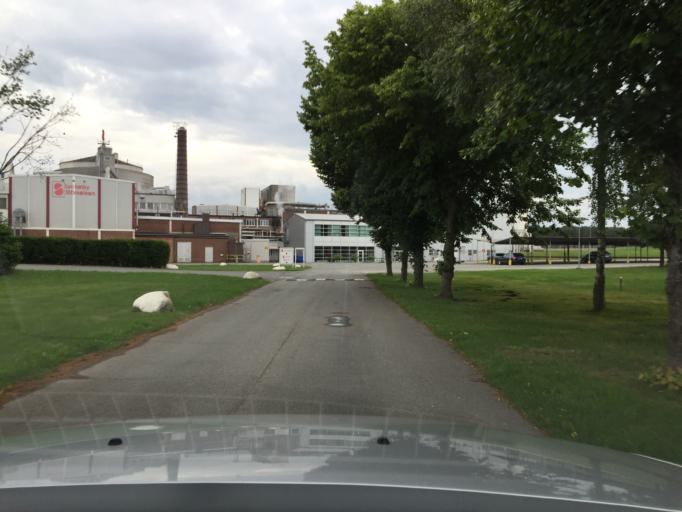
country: SE
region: Skane
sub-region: Kristianstads Kommun
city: Norra Asum
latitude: 55.9463
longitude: 14.0658
